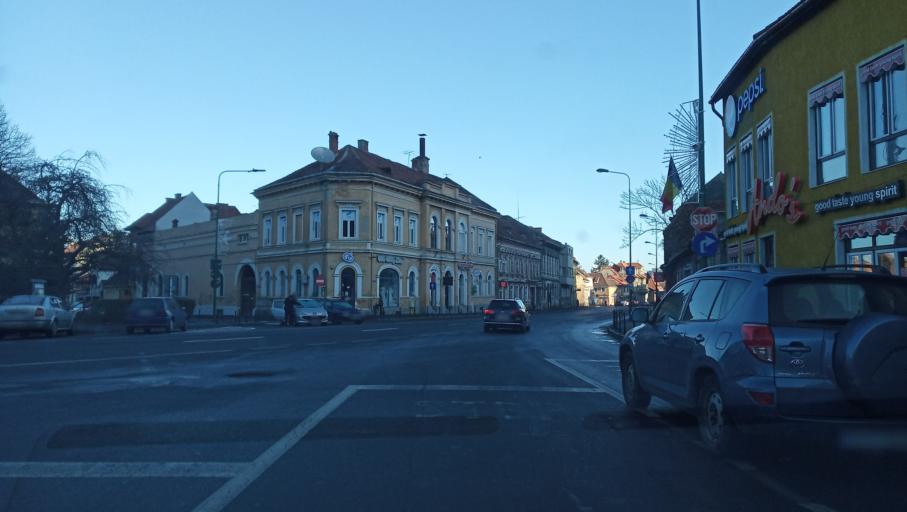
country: RO
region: Brasov
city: Brasov
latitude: 45.6454
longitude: 25.5992
